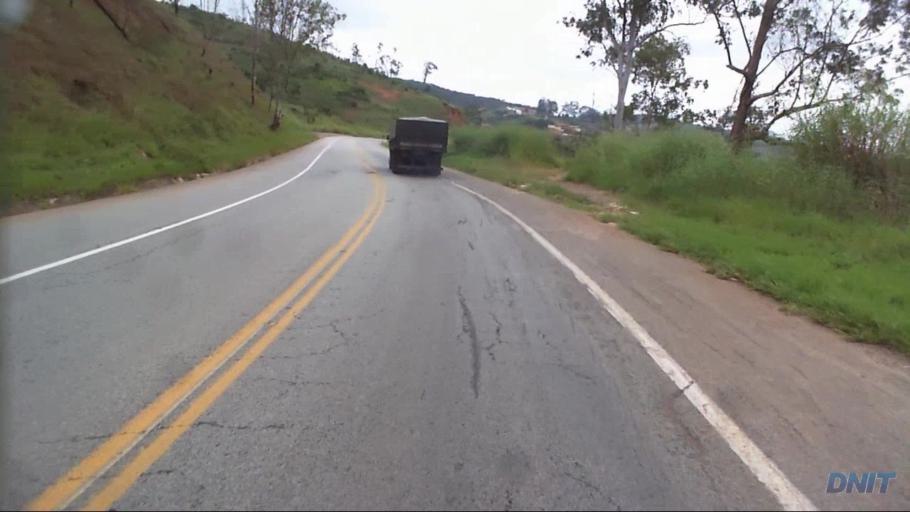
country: BR
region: Minas Gerais
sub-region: Nova Era
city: Nova Era
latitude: -19.8241
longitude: -43.0827
